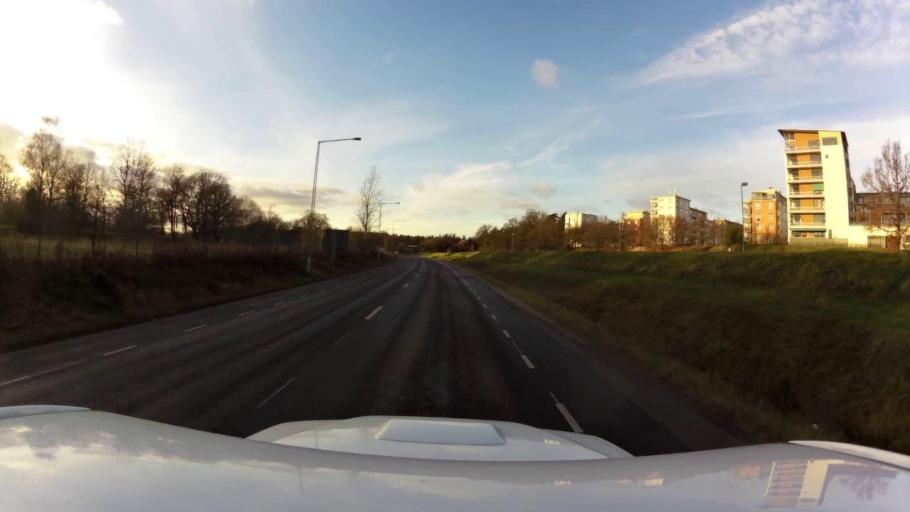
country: SE
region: OEstergoetland
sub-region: Linkopings Kommun
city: Linkoping
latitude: 58.3933
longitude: 15.6147
